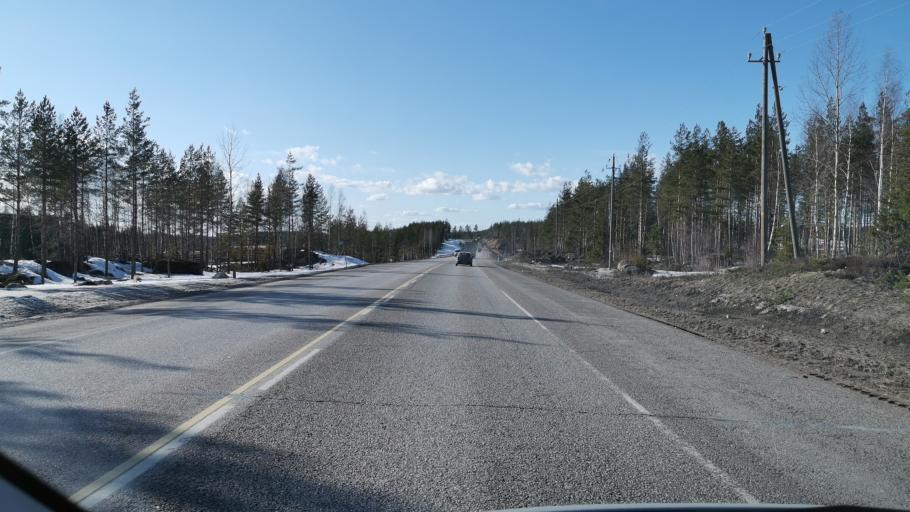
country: FI
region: Kymenlaakso
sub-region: Kouvola
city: Iitti
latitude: 60.8769
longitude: 26.4756
